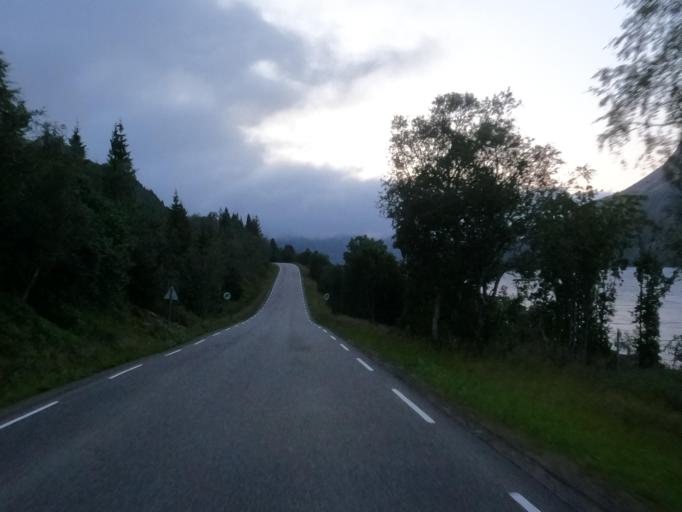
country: NO
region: Nordland
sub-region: Lodingen
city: Lodingen
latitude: 68.5887
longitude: 15.7907
